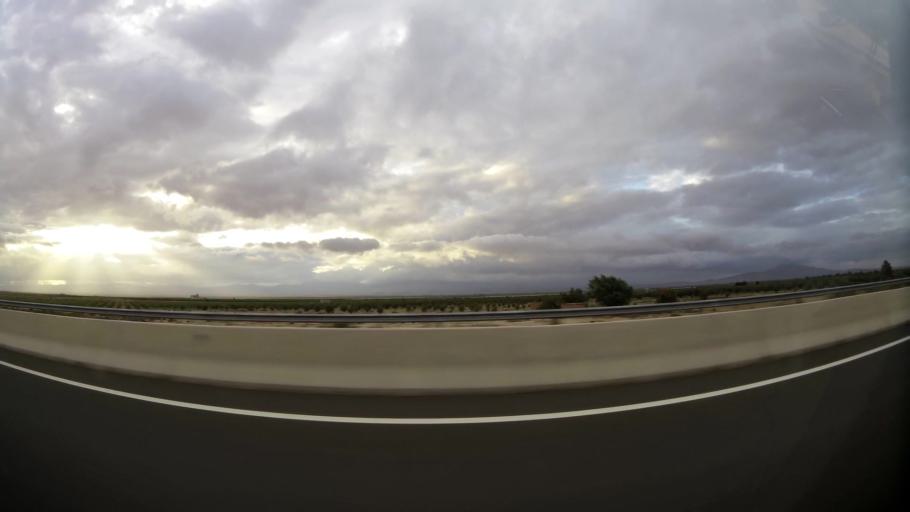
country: MA
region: Taza-Al Hoceima-Taounate
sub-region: Taza
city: Guercif
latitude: 34.3248
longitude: -3.3524
